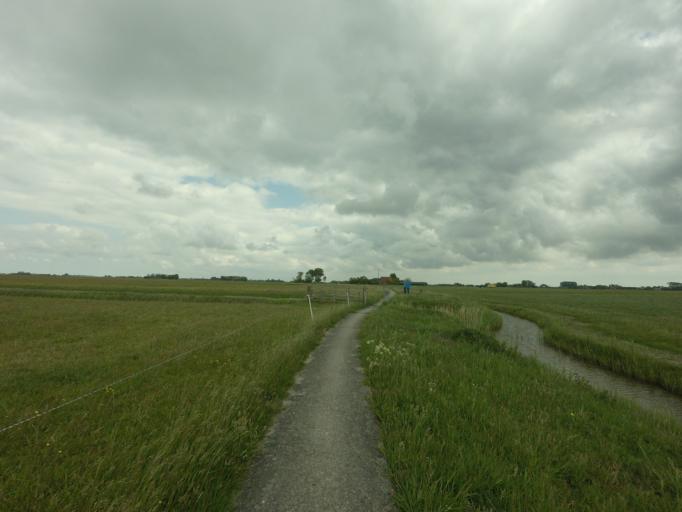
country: NL
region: Friesland
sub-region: Gemeente Littenseradiel
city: Wommels
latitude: 53.1089
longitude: 5.6060
